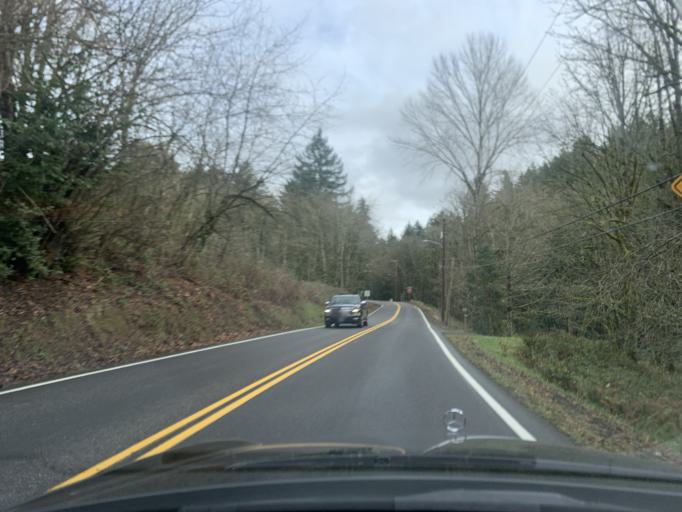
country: US
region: Oregon
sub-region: Multnomah County
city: Gresham
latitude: 45.4705
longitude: -122.4499
